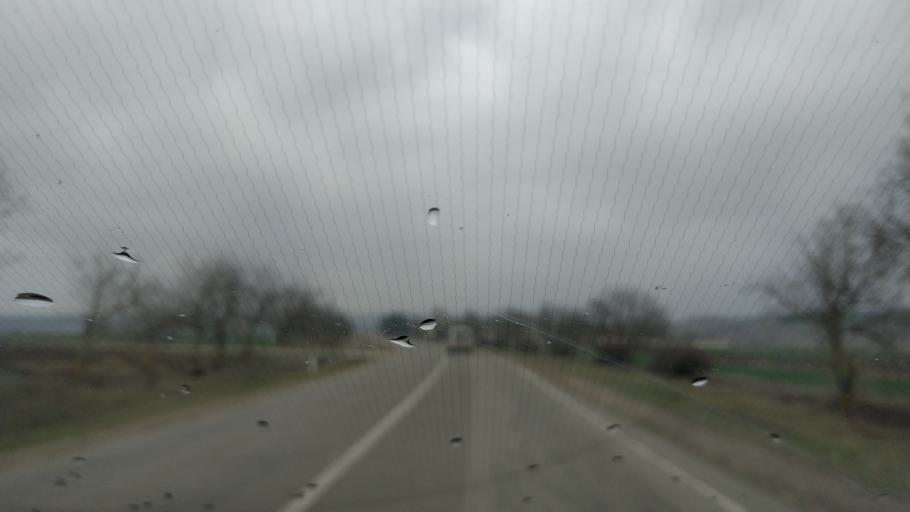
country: MD
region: Gagauzia
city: Comrat
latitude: 46.2485
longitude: 28.7598
